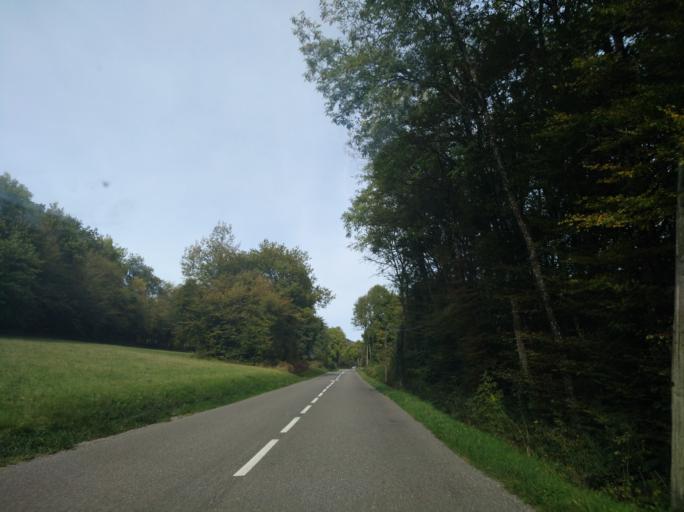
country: FR
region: Bourgogne
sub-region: Departement de Saone-et-Loire
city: Cuiseaux
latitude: 46.4597
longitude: 5.3985
